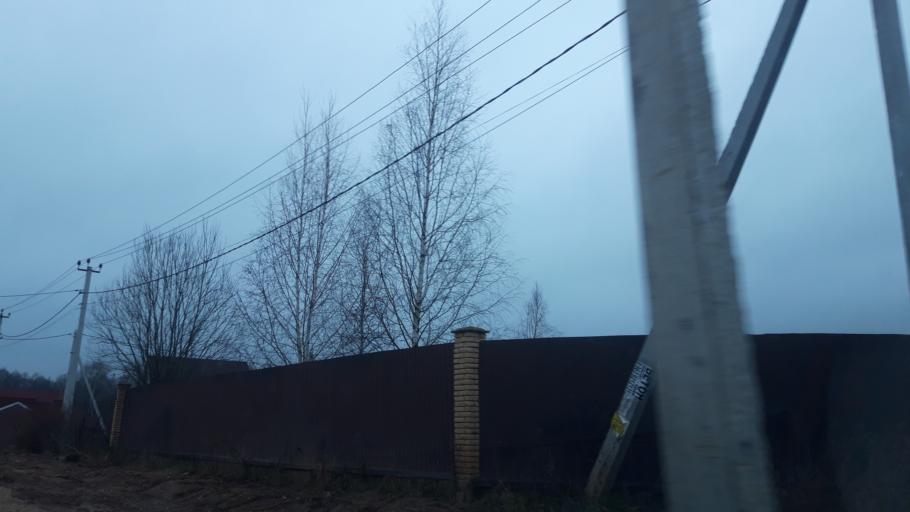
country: RU
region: Moskovskaya
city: Solnechnogorsk
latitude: 56.0788
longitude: 36.9245
